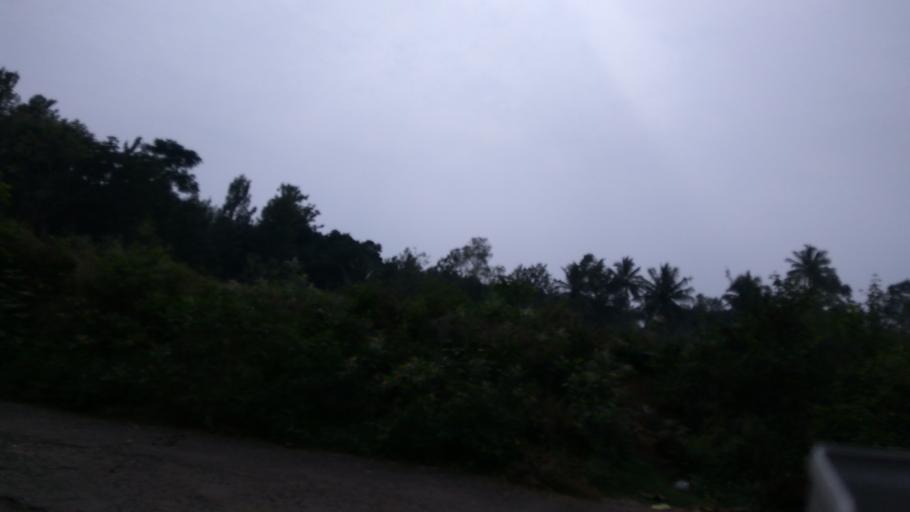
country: IN
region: Tamil Nadu
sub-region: Dharmapuri
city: Mallapuram
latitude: 11.8673
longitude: 78.1923
